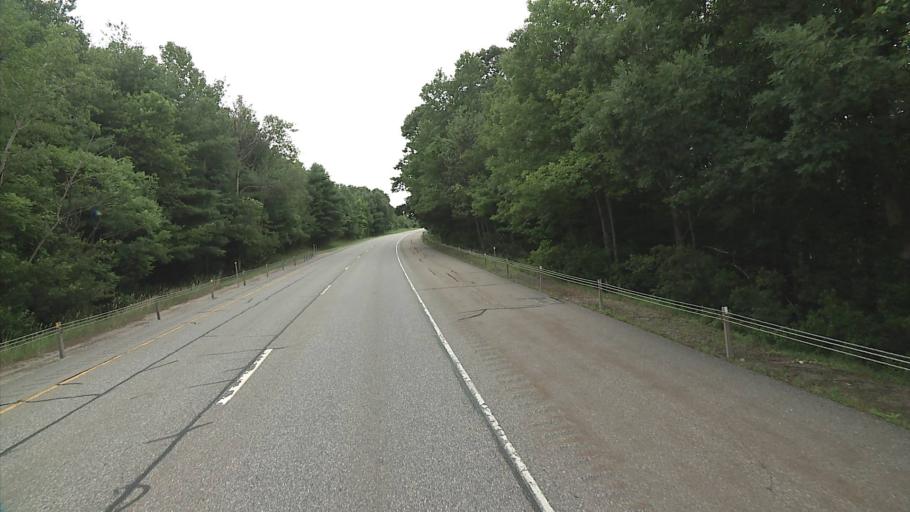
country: US
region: Connecticut
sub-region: Litchfield County
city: Torrington
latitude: 41.8418
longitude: -73.0969
